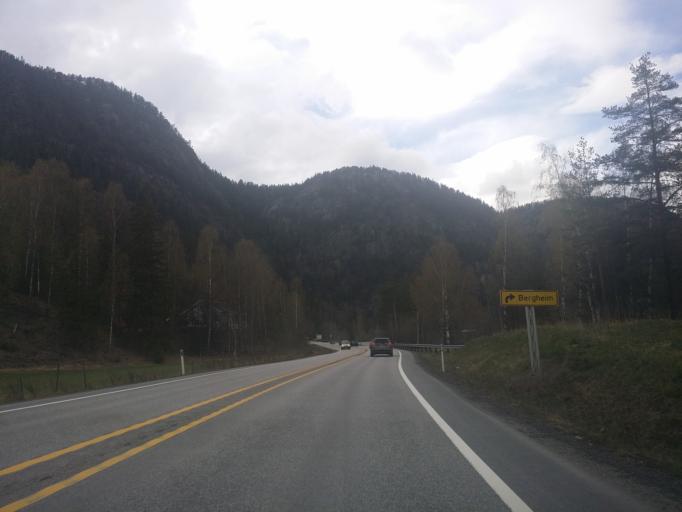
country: NO
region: Buskerud
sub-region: Nes
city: Nesbyen
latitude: 60.4708
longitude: 9.2342
